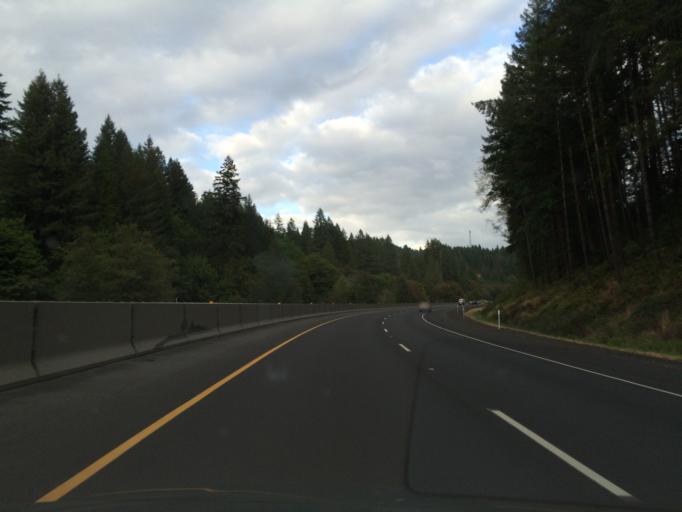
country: US
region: Oregon
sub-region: Lane County
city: Cottage Grove
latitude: 43.7524
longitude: -123.1627
